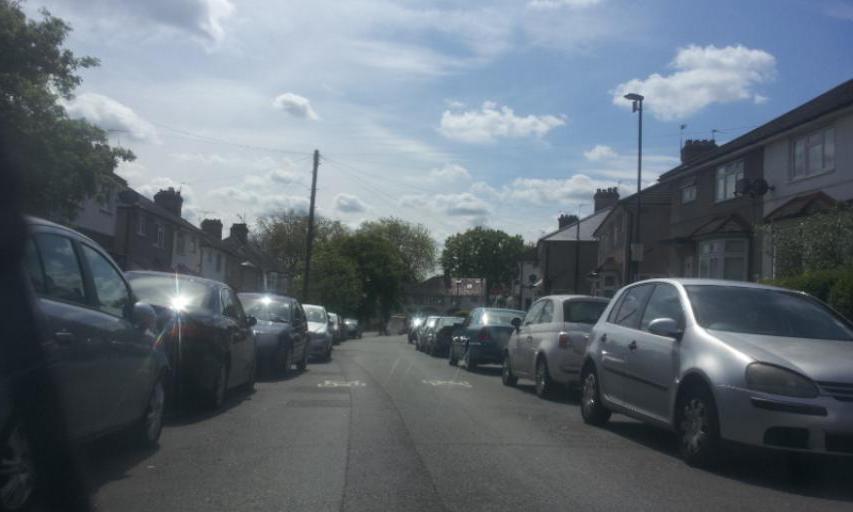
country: GB
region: England
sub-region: Greater London
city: Catford
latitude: 51.4502
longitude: -0.0291
